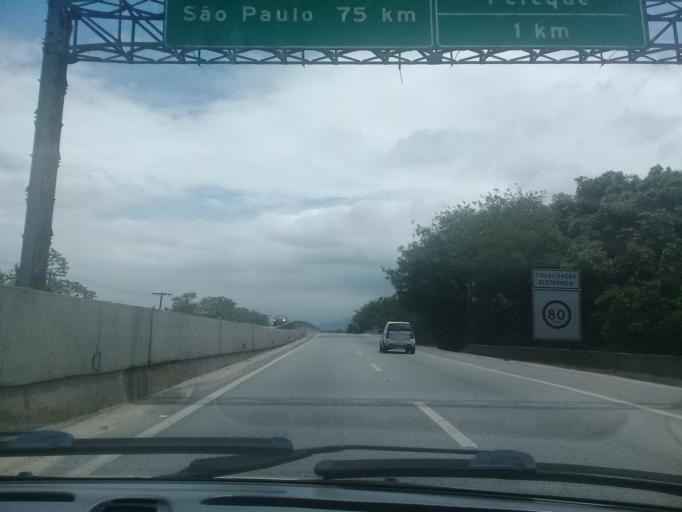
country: BR
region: Sao Paulo
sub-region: Guaruja
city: Guaruja
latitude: -23.9806
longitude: -46.2662
